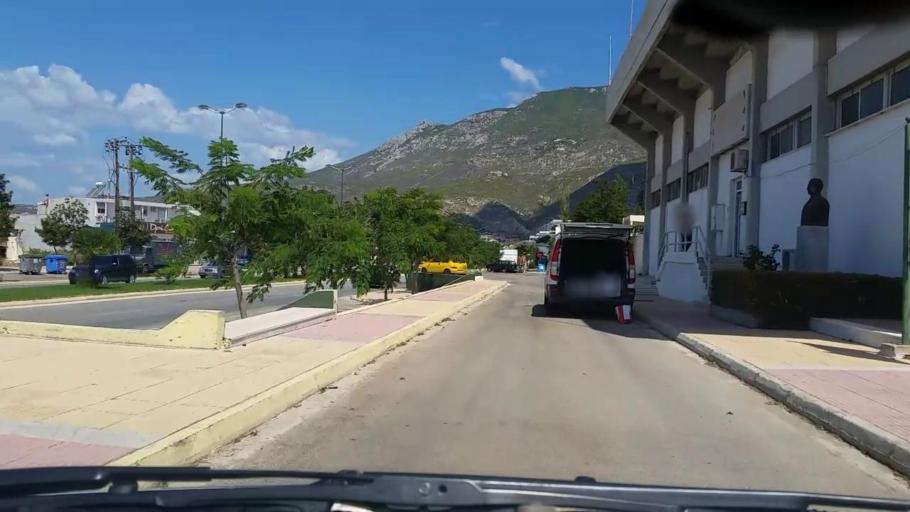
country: GR
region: Peloponnese
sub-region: Nomos Korinthias
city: Loutraki
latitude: 37.9656
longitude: 22.9786
